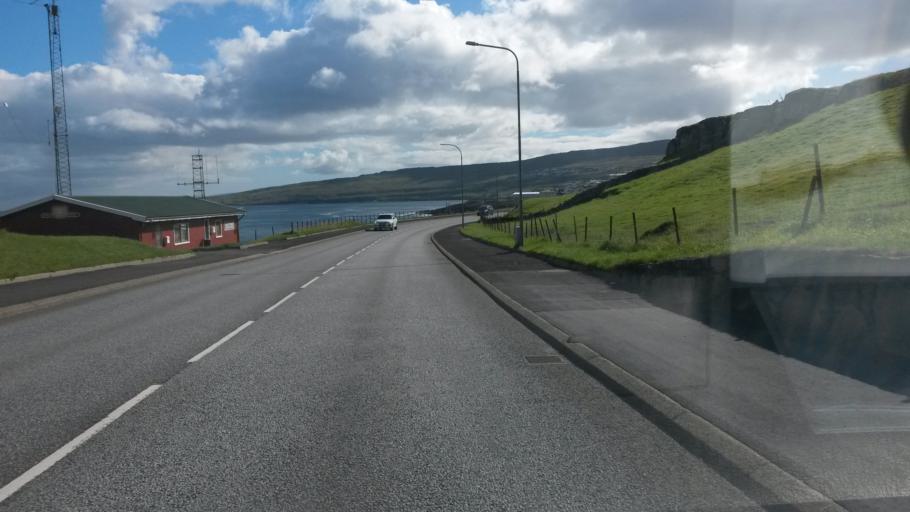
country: FO
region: Streymoy
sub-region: Torshavn
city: Torshavn
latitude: 62.0161
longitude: -6.7555
